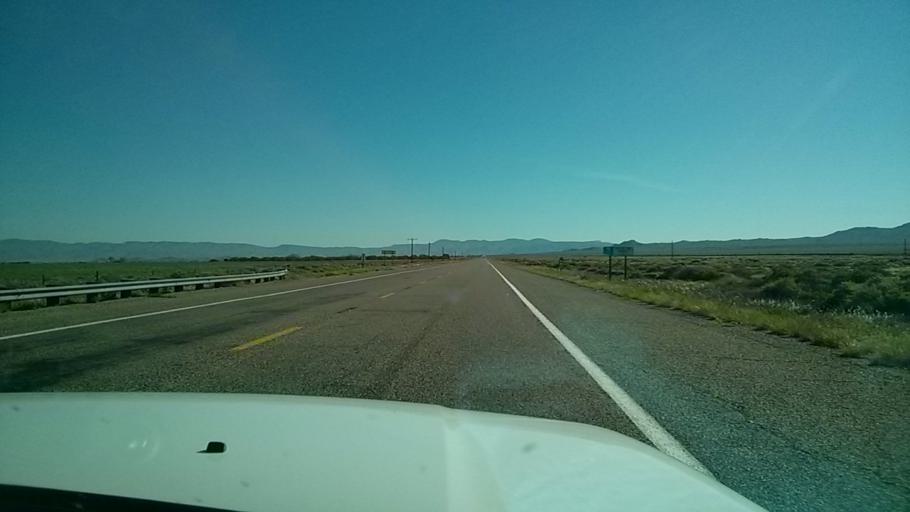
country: US
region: Arizona
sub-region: Mohave County
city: New Kingman-Butler
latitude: 35.3456
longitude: -113.8878
